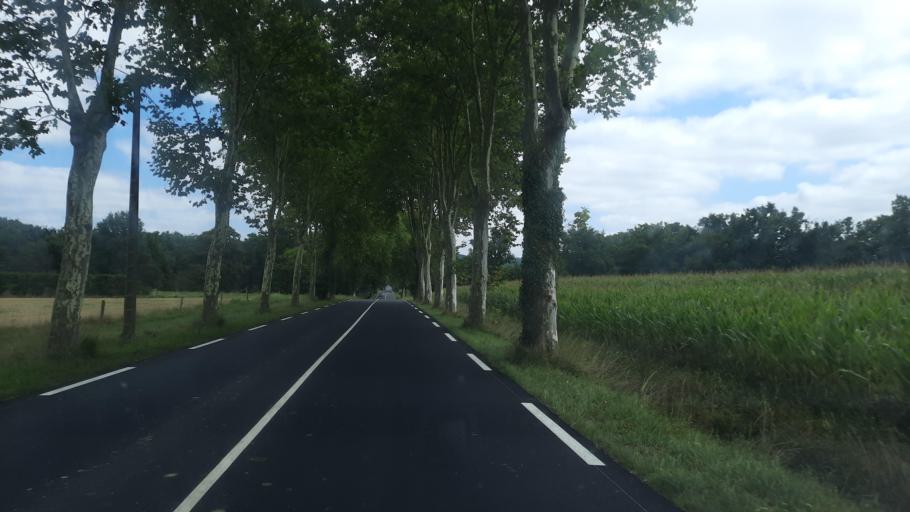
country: FR
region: Midi-Pyrenees
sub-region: Departement de la Haute-Garonne
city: Boulogne-sur-Gesse
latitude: 43.2906
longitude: 0.5278
